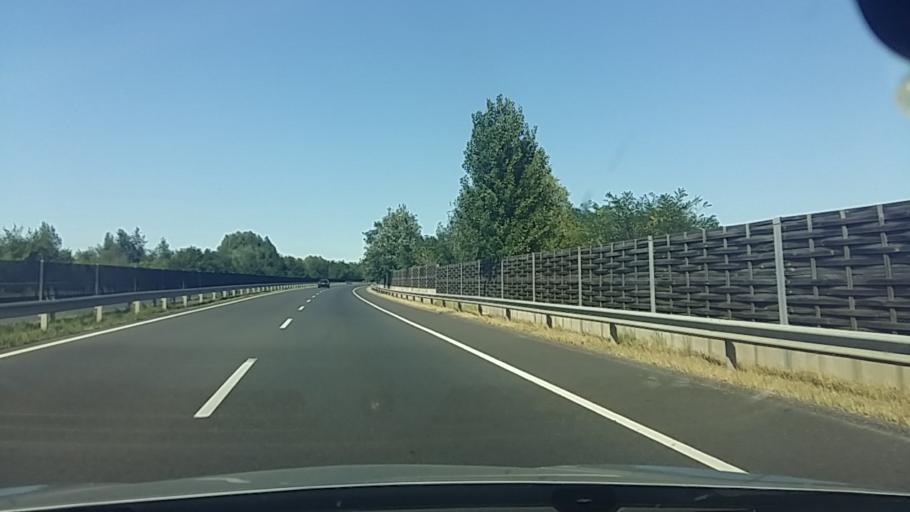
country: HU
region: Szabolcs-Szatmar-Bereg
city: Nyiregyhaza
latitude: 47.8908
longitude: 21.7102
